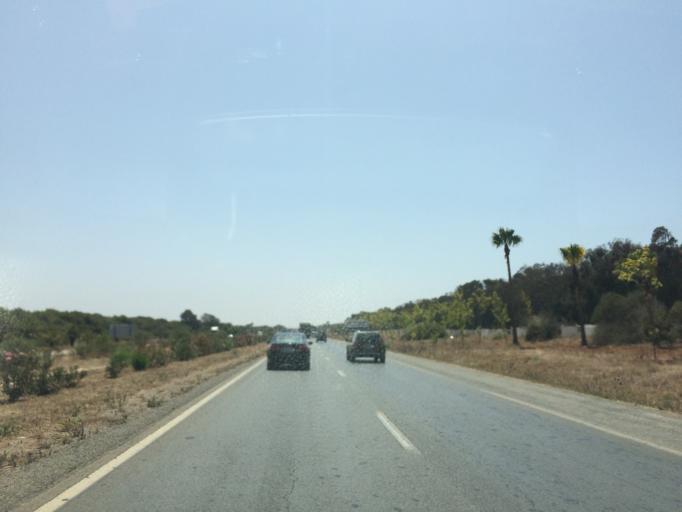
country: MA
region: Rabat-Sale-Zemmour-Zaer
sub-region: Skhirate-Temara
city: Temara
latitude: 33.9577
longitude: -6.9100
